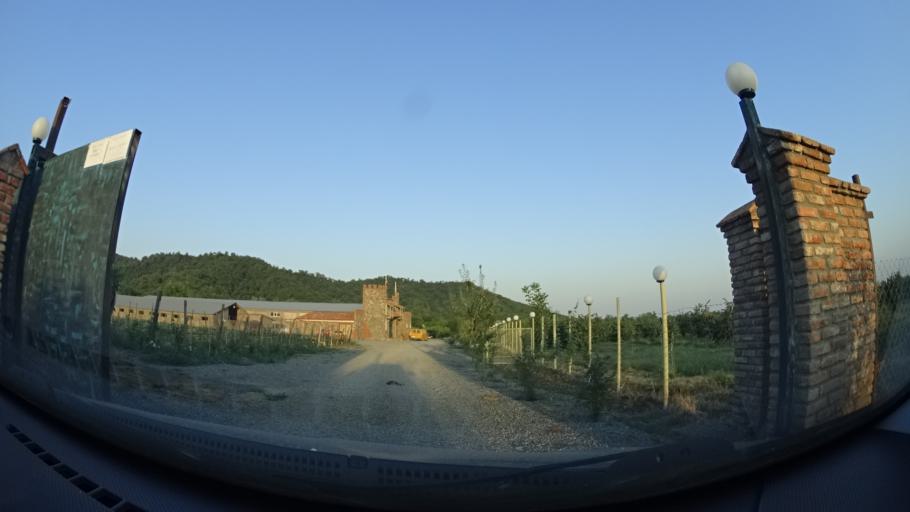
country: GE
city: Bagdadi
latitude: 41.8661
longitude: 46.0185
